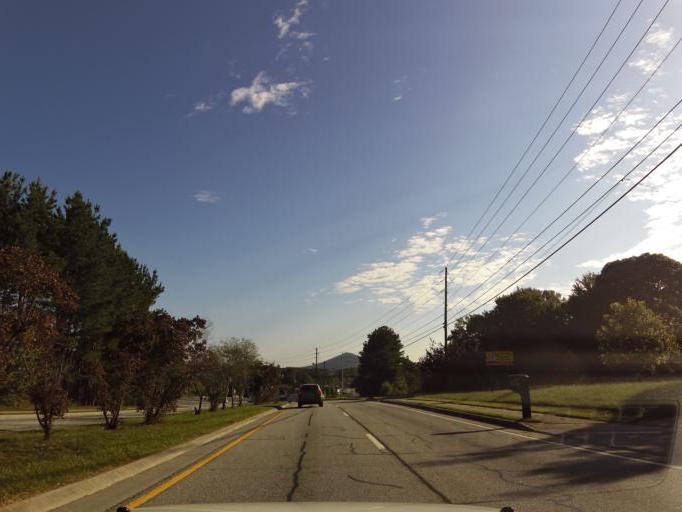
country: US
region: Georgia
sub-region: Cobb County
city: Marietta
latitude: 33.9428
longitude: -84.6255
